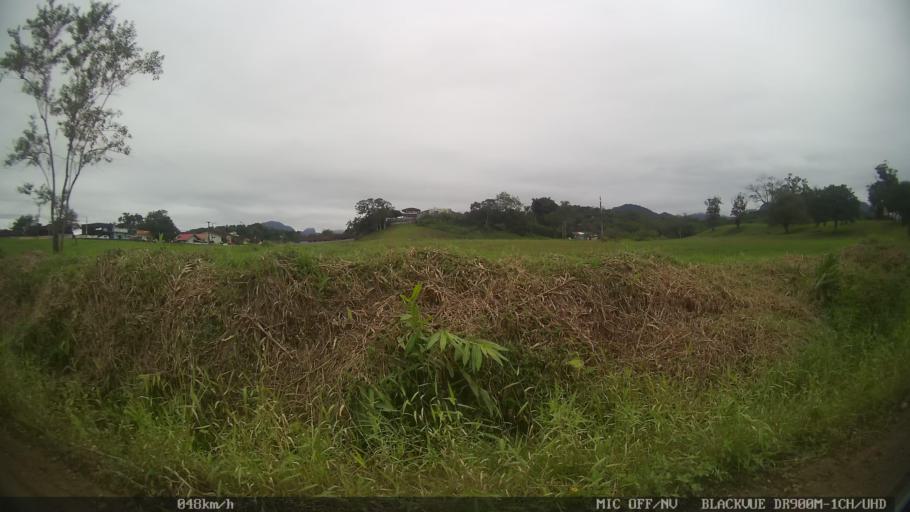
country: BR
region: Santa Catarina
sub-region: Joinville
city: Joinville
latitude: -26.2768
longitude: -48.9092
